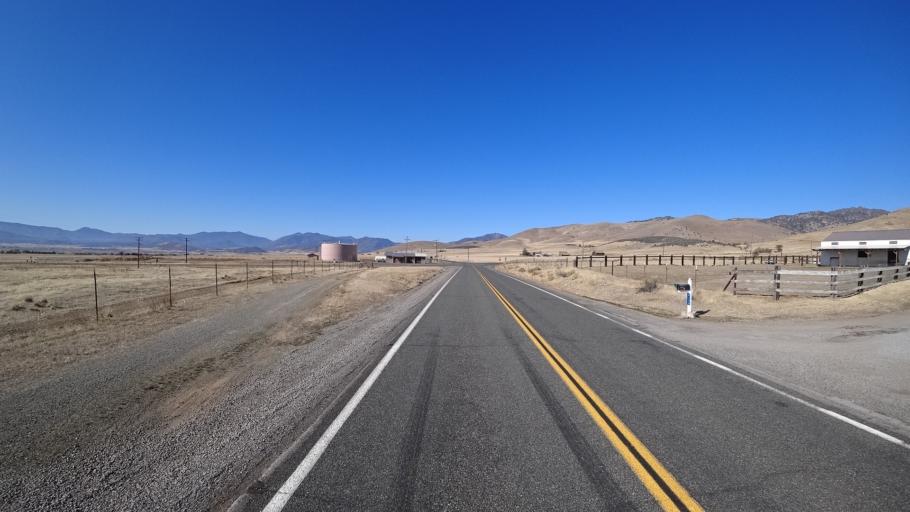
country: US
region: California
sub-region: Siskiyou County
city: Montague
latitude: 41.7709
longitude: -122.5208
